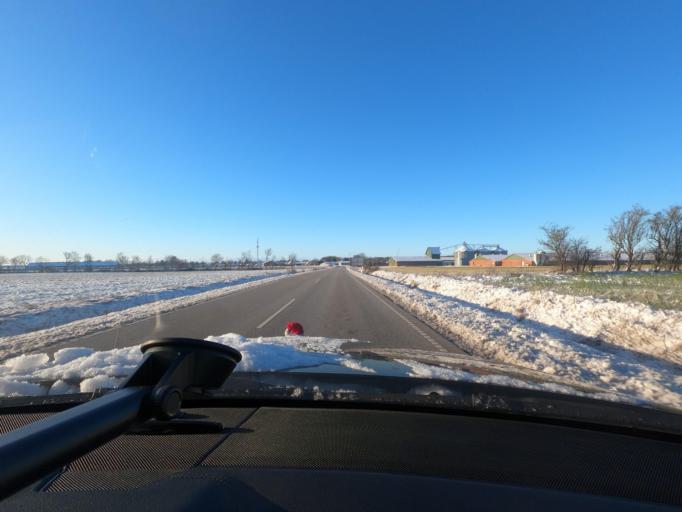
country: DK
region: South Denmark
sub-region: Aabenraa Kommune
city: Rodekro
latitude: 55.0767
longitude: 9.2262
